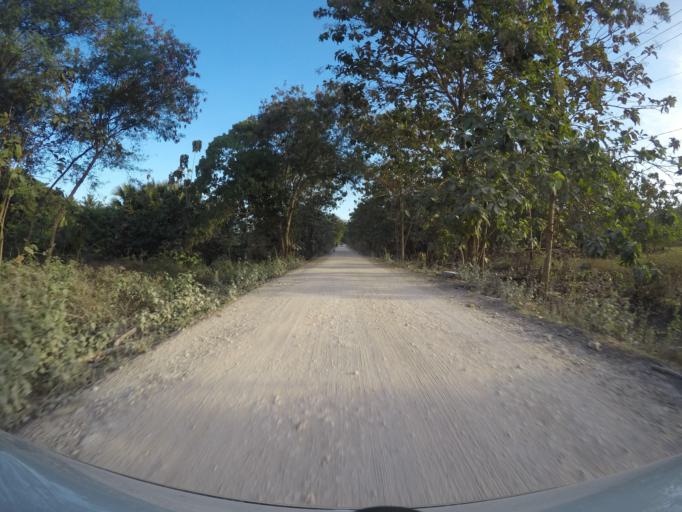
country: TL
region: Viqueque
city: Viqueque
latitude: -8.8812
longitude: 126.5074
